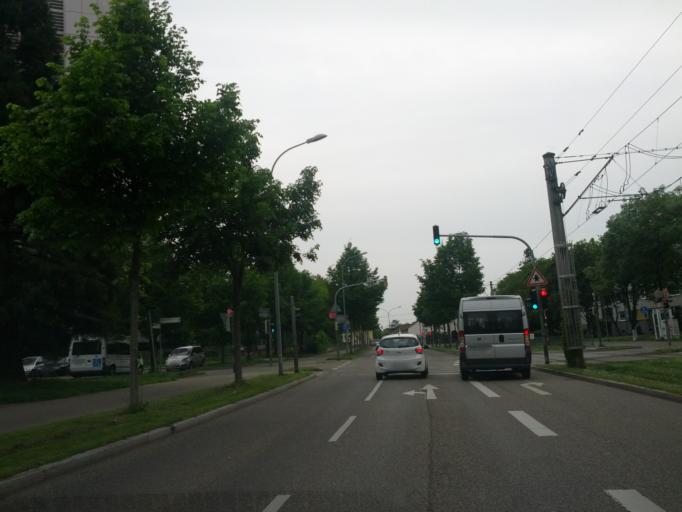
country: DE
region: Baden-Wuerttemberg
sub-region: Freiburg Region
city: Merzhausen
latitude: 47.9958
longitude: 7.8051
